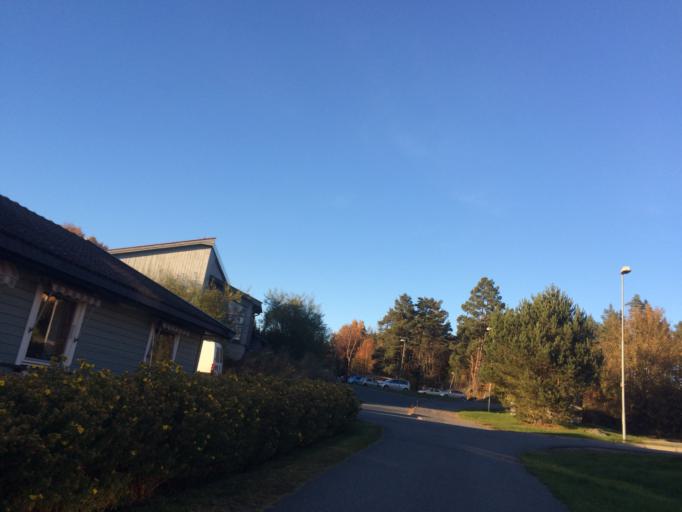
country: NO
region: Akershus
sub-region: Ski
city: Ski
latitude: 59.7253
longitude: 10.8633
